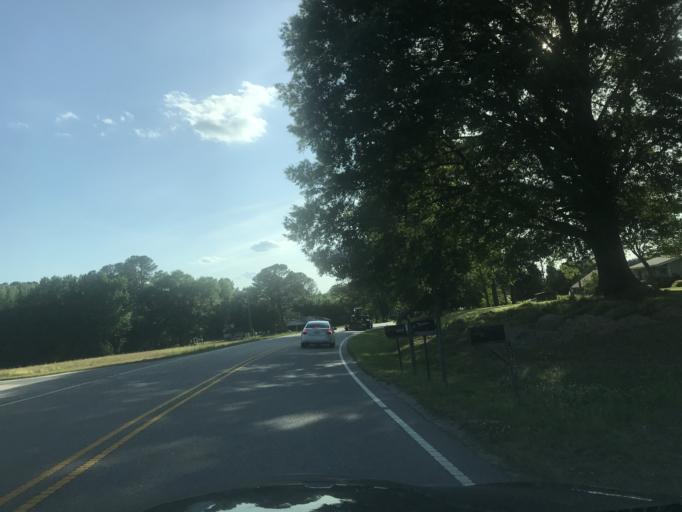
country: US
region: North Carolina
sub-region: Wake County
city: Wendell
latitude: 35.7635
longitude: -78.4128
